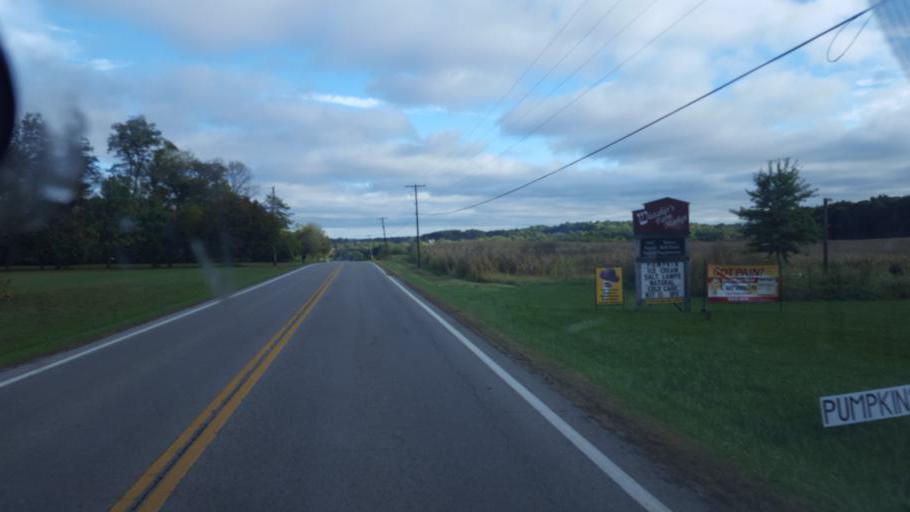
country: US
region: Ohio
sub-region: Sandusky County
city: Bellville
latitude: 40.5587
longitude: -82.5353
